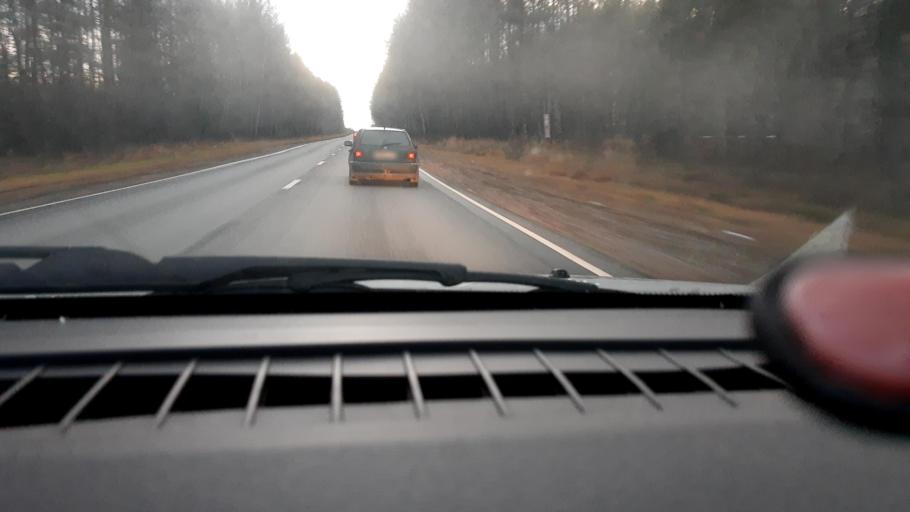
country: RU
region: Nizjnij Novgorod
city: Krasnyye Baki
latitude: 57.0415
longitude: 45.1290
